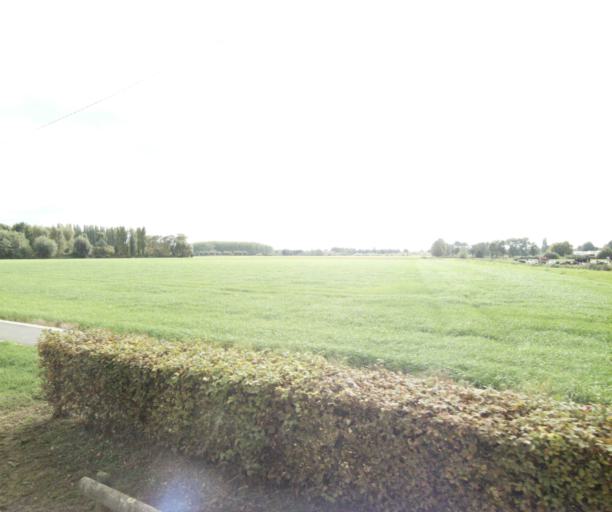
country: FR
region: Nord-Pas-de-Calais
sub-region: Departement du Nord
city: Premesques
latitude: 50.6635
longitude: 2.9389
